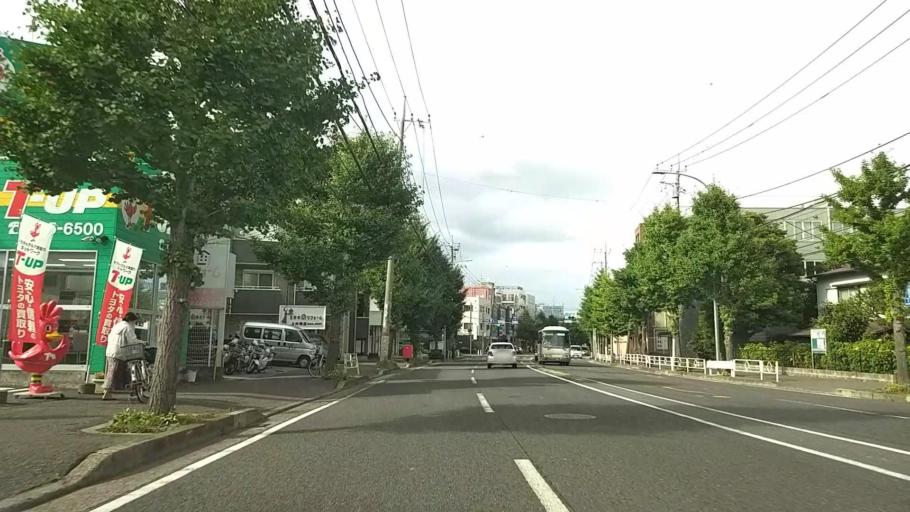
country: JP
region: Kanagawa
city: Yokohama
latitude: 35.3970
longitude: 139.5868
